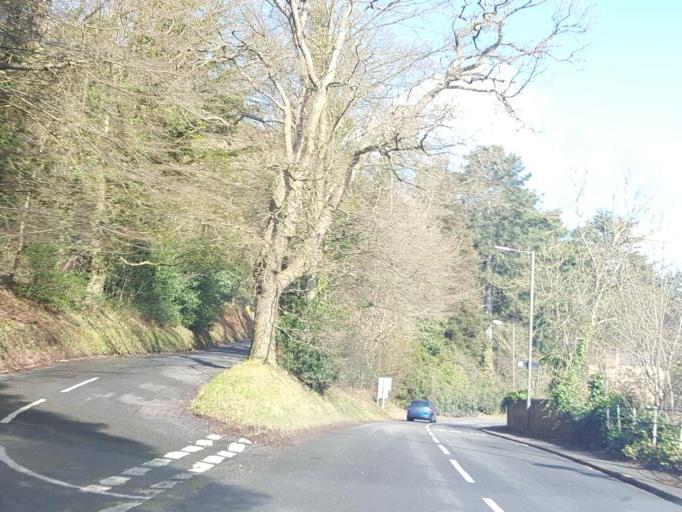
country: GB
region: England
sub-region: Worcestershire
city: Great Malvern
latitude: 52.1029
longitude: -2.3302
